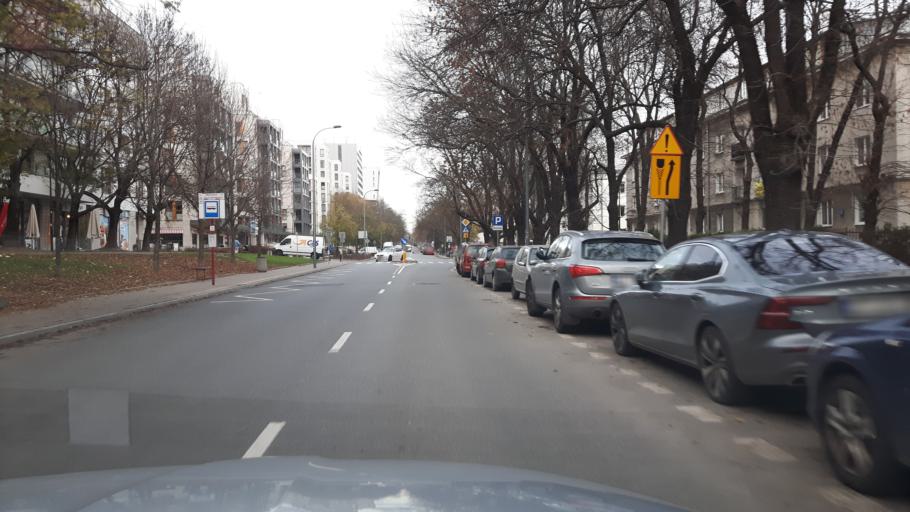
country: PL
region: Masovian Voivodeship
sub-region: Warszawa
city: Mokotow
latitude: 52.1719
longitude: 20.9989
